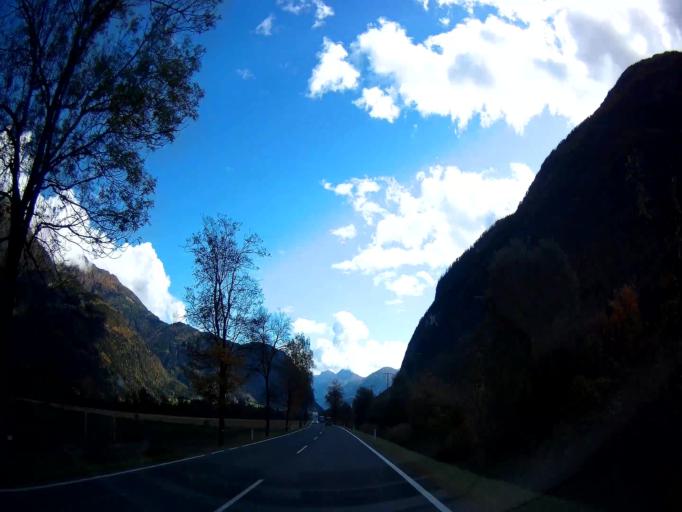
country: AT
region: Tyrol
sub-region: Politischer Bezirk Lienz
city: Nikolsdorf
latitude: 46.7841
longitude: 12.8843
